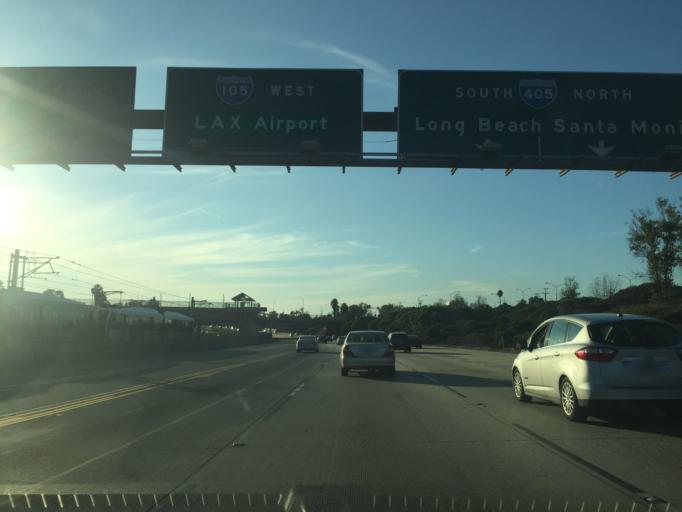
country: US
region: California
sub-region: Los Angeles County
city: Lennox
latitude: 33.9331
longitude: -118.3493
